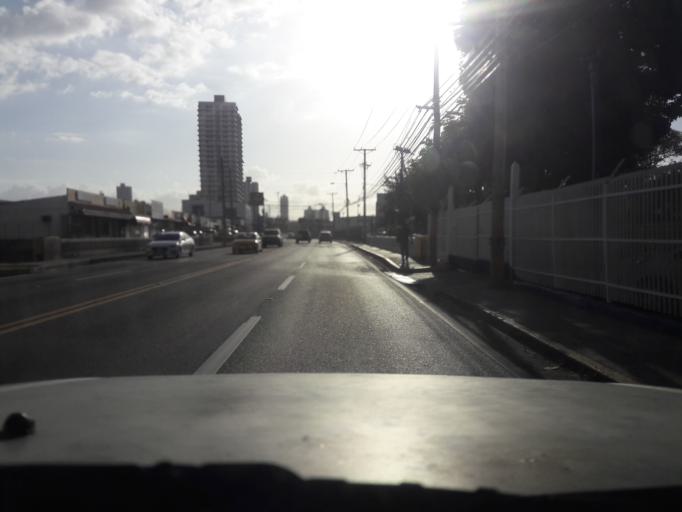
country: PA
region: Panama
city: Panama
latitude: 9.0161
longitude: -79.4969
